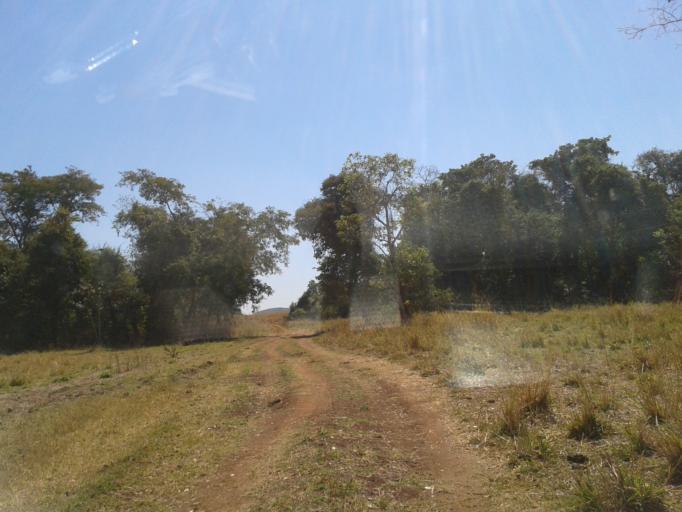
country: BR
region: Minas Gerais
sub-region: Santa Vitoria
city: Santa Vitoria
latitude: -19.0753
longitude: -50.0346
